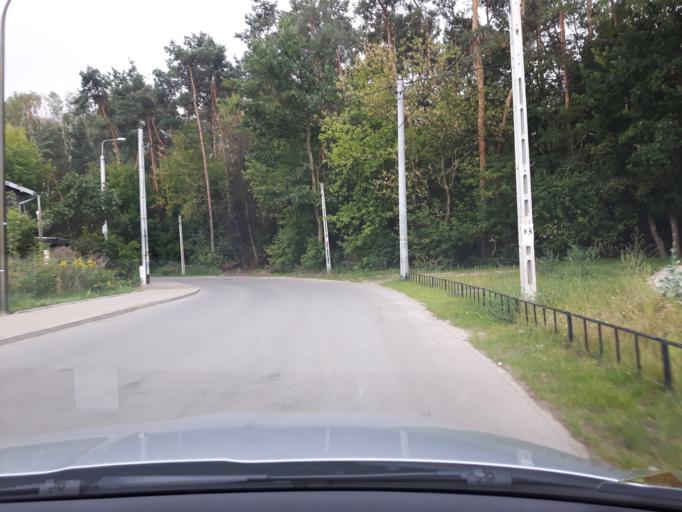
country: PL
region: Masovian Voivodeship
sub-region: Warszawa
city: Praga Poludnie
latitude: 52.2520
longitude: 21.1218
